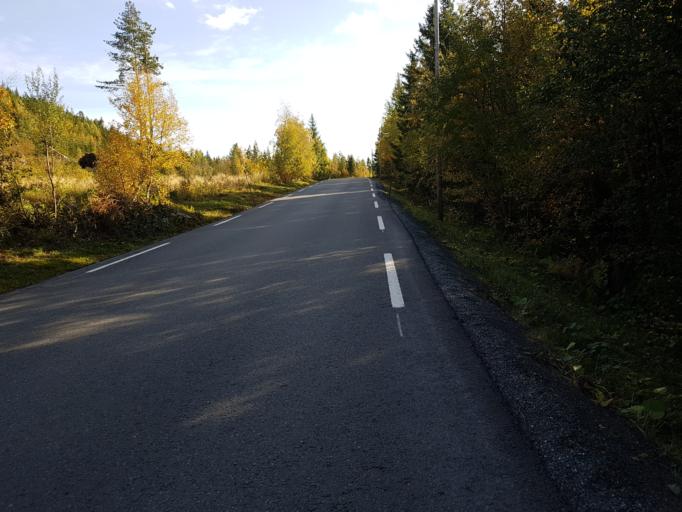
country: NO
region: Sor-Trondelag
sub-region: Malvik
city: Malvik
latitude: 63.3712
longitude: 10.6147
